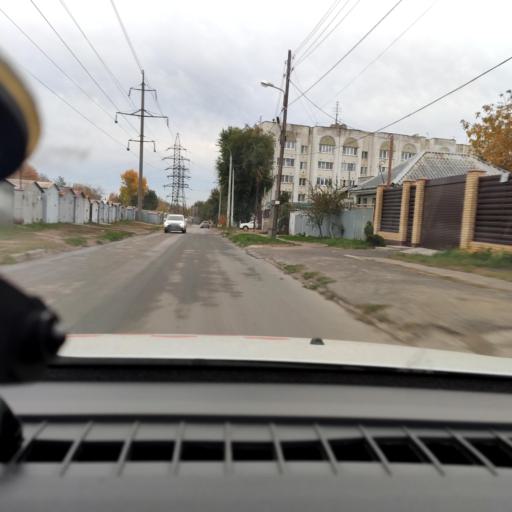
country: RU
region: Samara
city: Samara
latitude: 53.1927
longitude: 50.2201
